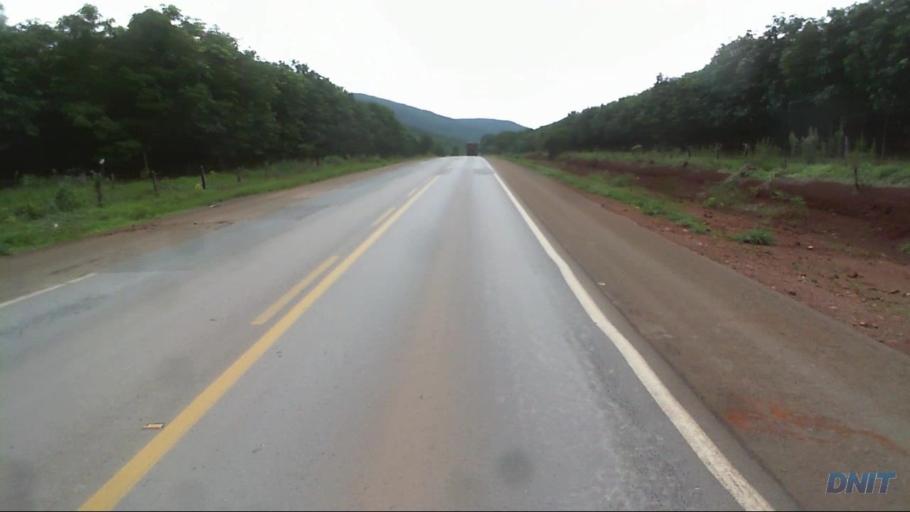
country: BR
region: Goias
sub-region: Barro Alto
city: Barro Alto
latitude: -14.8821
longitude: -48.9870
